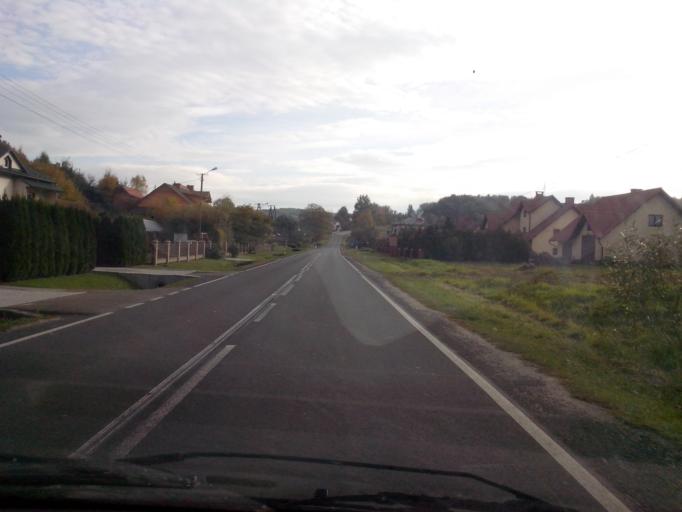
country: PL
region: Subcarpathian Voivodeship
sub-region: Powiat ropczycko-sedziszowski
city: Wielopole Skrzynskie
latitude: 49.9426
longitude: 21.6156
